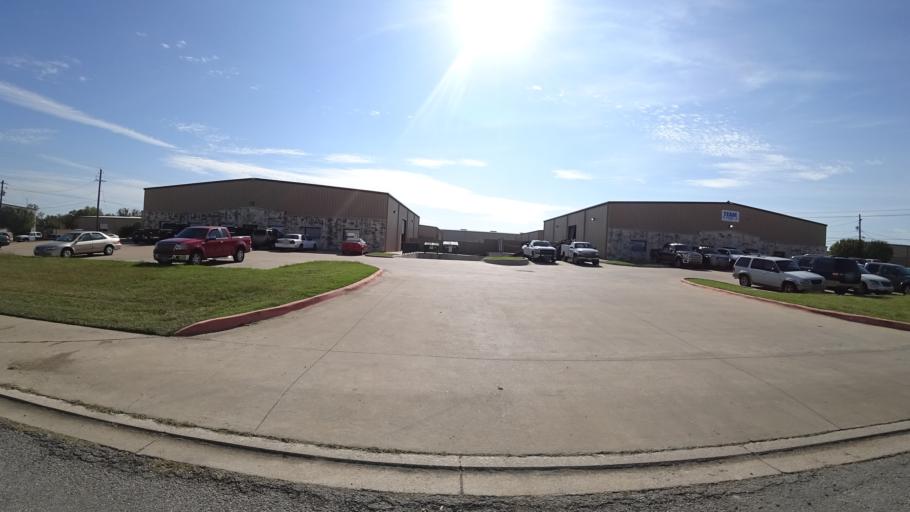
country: US
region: Texas
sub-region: Travis County
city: Pflugerville
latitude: 30.4044
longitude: -97.6281
